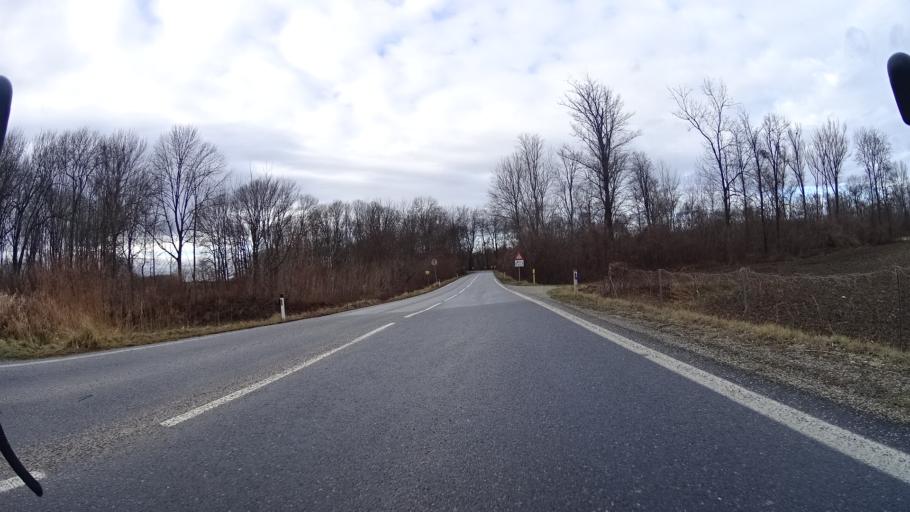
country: AT
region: Lower Austria
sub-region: Politischer Bezirk Tulln
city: Langenrohr
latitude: 48.3272
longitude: 16.0269
